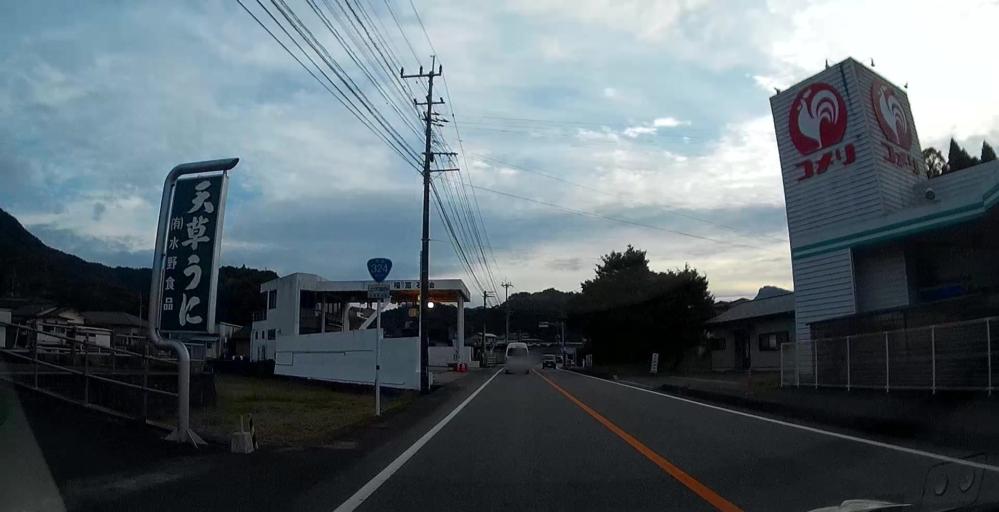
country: JP
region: Kumamoto
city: Yatsushiro
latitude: 32.5024
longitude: 130.4269
